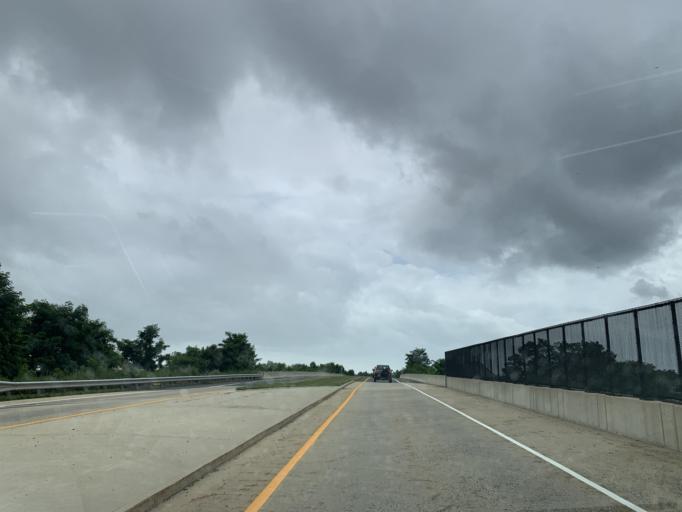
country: US
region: New Jersey
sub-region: Somerset County
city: Bloomingdale
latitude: 40.4889
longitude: -74.6391
